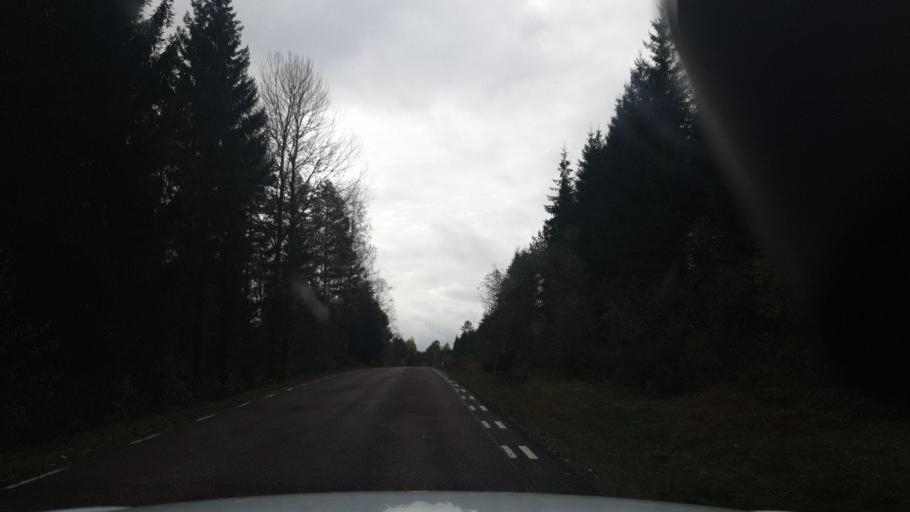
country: SE
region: Vaermland
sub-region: Karlstads Kommun
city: Edsvalla
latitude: 59.5208
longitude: 13.1121
